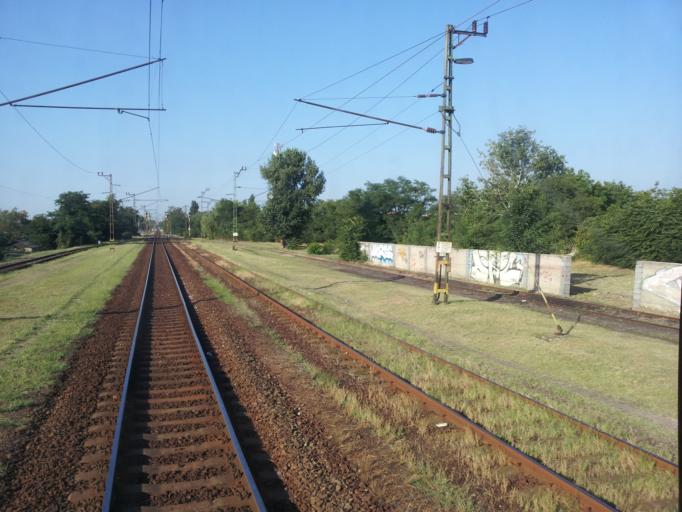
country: HU
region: Pest
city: Dunaharaszti
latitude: 47.3503
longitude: 19.0950
